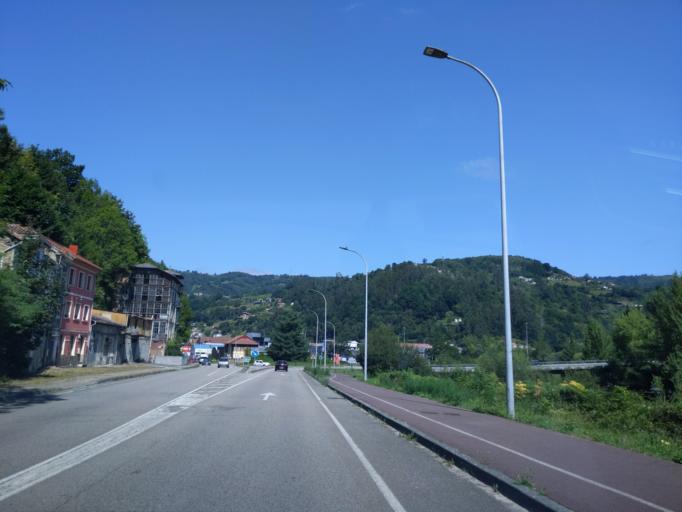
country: ES
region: Asturias
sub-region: Province of Asturias
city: El entrego
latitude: 43.2836
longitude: -5.6243
